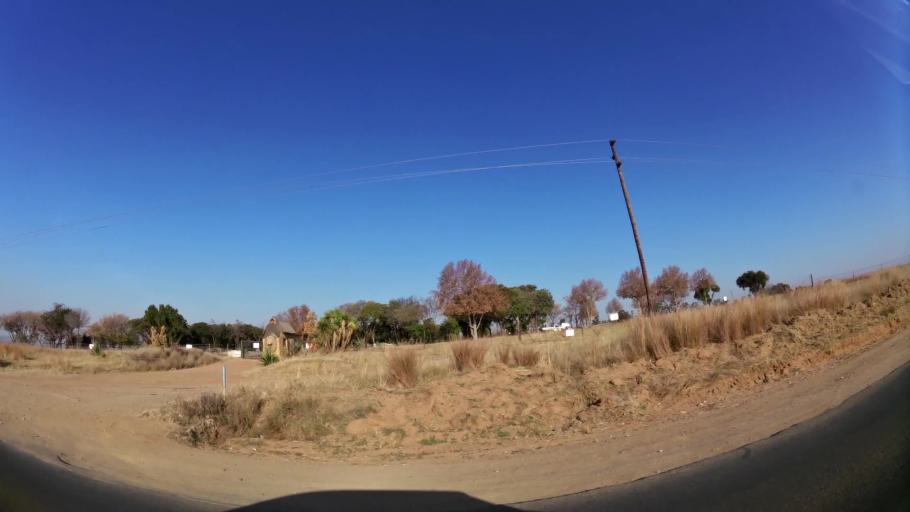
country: ZA
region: Gauteng
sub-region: West Rand District Municipality
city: Muldersdriseloop
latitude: -25.9930
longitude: 27.9298
